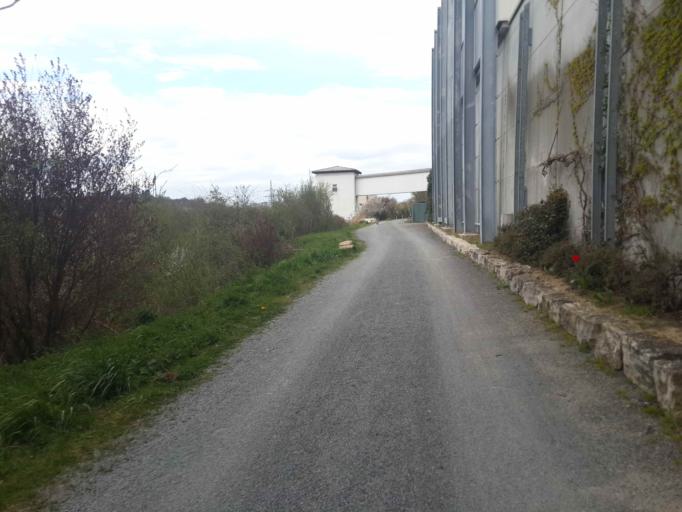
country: DE
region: Baden-Wuerttemberg
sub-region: Regierungsbezirk Stuttgart
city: Untereisesheim
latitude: 49.2193
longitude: 9.2071
